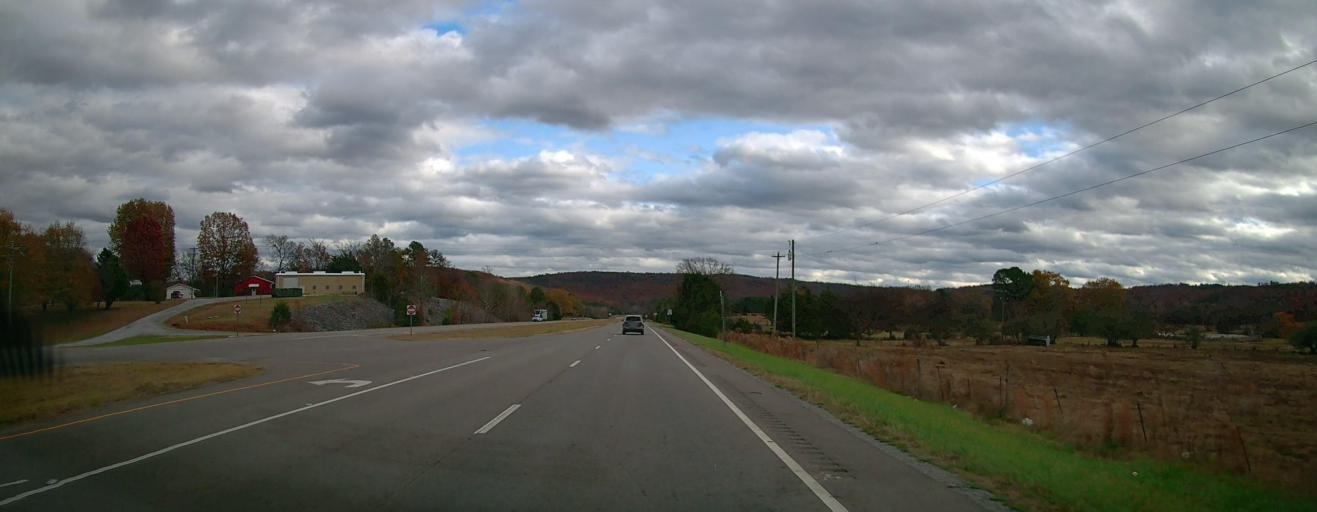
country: US
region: Alabama
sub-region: Morgan County
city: Danville
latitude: 34.3354
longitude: -87.0171
